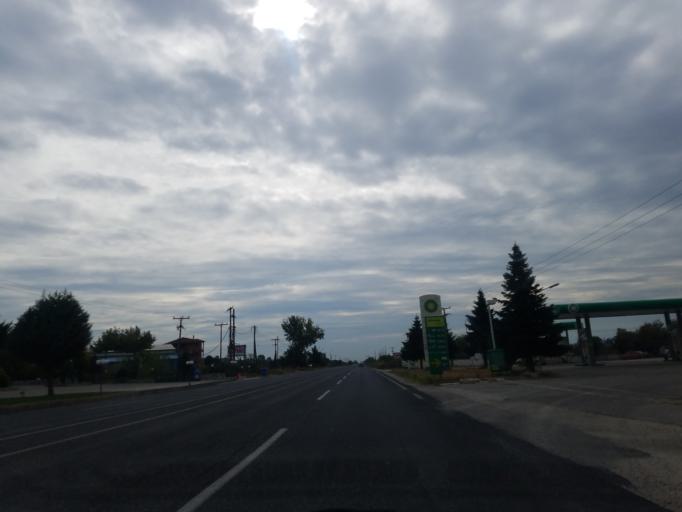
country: GR
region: Thessaly
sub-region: Trikala
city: Kalampaka
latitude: 39.6867
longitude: 21.6492
